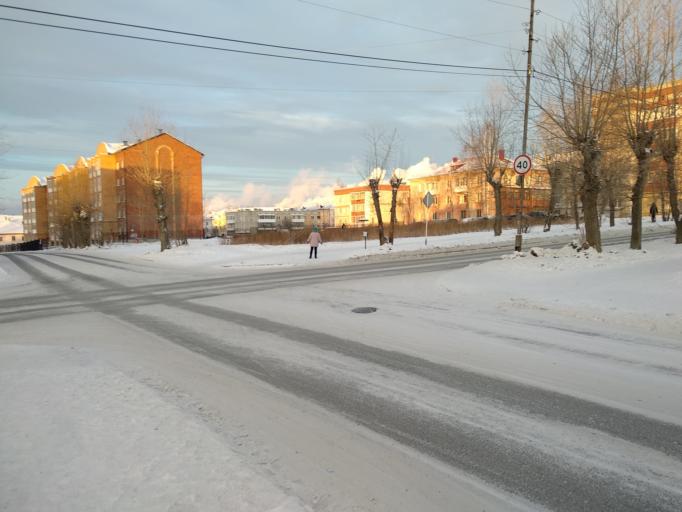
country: RU
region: Sverdlovsk
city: Krasnotur'insk
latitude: 59.7615
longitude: 60.2058
